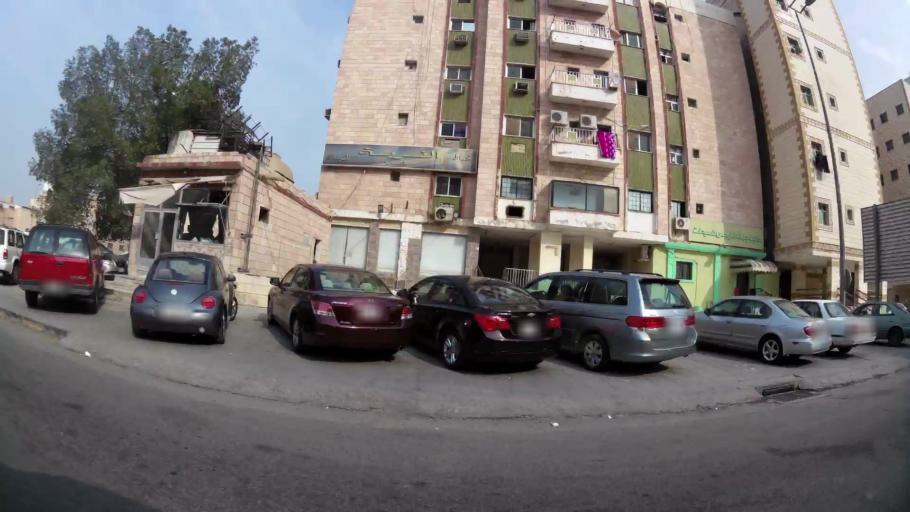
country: KW
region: Al Farwaniyah
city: Al Farwaniyah
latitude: 29.2890
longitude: 47.9548
